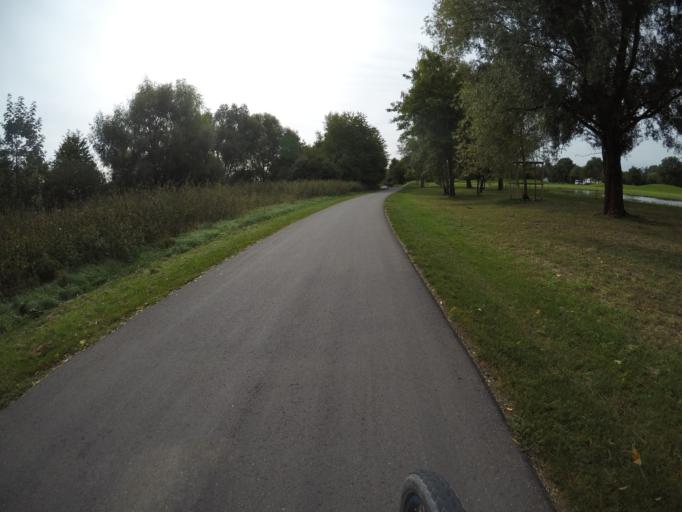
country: DE
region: Baden-Wuerttemberg
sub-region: Karlsruhe Region
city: Sankt Leon-Rot
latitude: 49.2467
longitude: 8.6298
